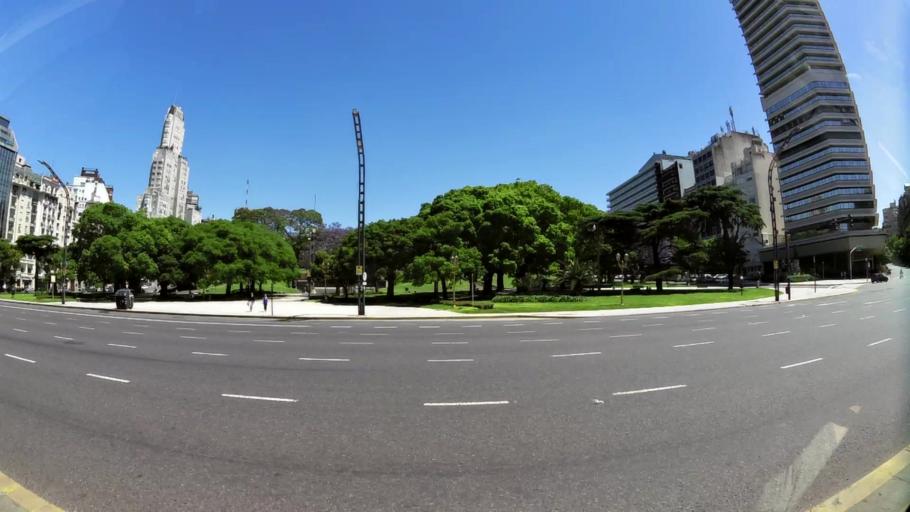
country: AR
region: Buenos Aires F.D.
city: Retiro
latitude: -34.5931
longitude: -58.3747
